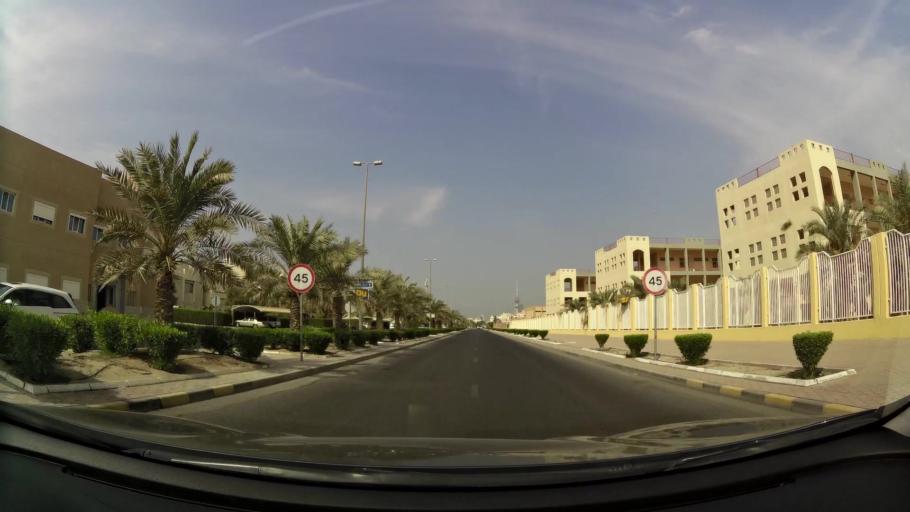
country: KW
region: Al Asimah
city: Ash Shamiyah
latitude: 29.3366
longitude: 47.9768
